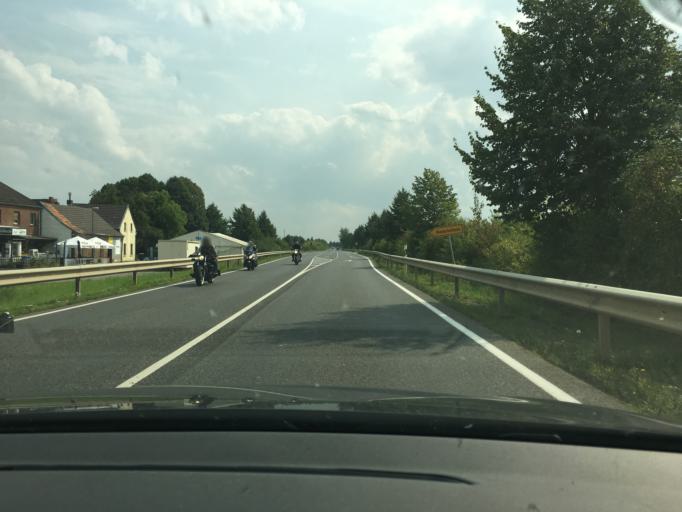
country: DE
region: North Rhine-Westphalia
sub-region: Regierungsbezirk Koln
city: Norvenich
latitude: 50.8313
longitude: 6.6275
